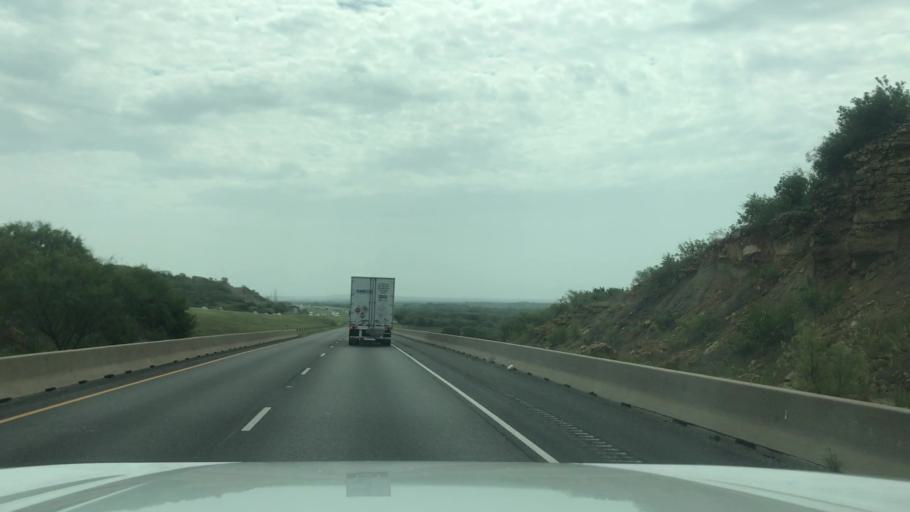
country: US
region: Texas
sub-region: Callahan County
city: Baird
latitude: 32.3946
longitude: -99.3606
